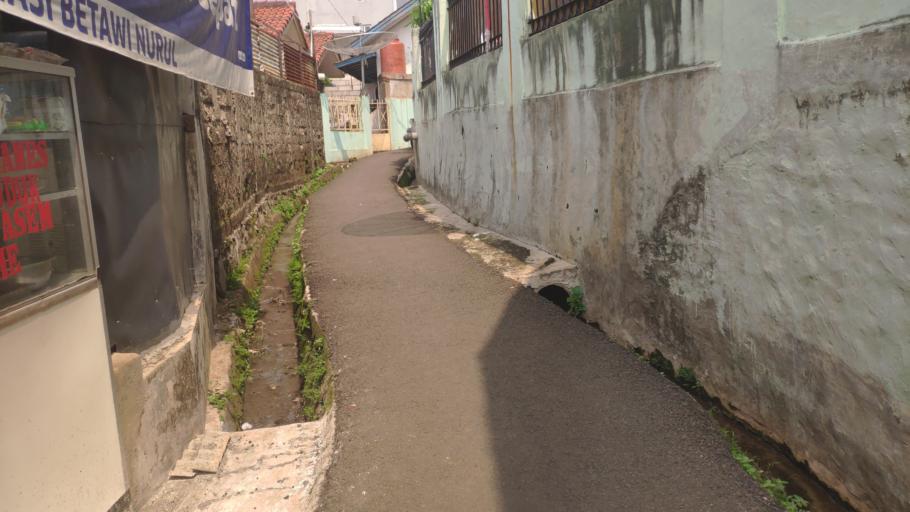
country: ID
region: Jakarta Raya
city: Jakarta
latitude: -6.2680
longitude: 106.8298
